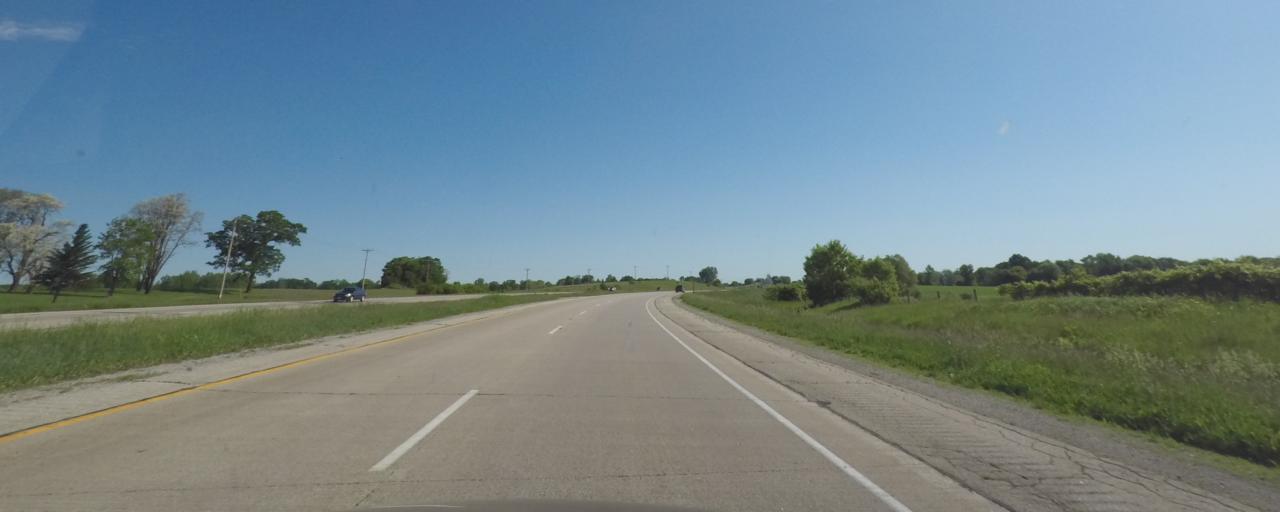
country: US
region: Wisconsin
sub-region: Fond du Lac County
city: Waupun
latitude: 43.5645
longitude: -88.7751
